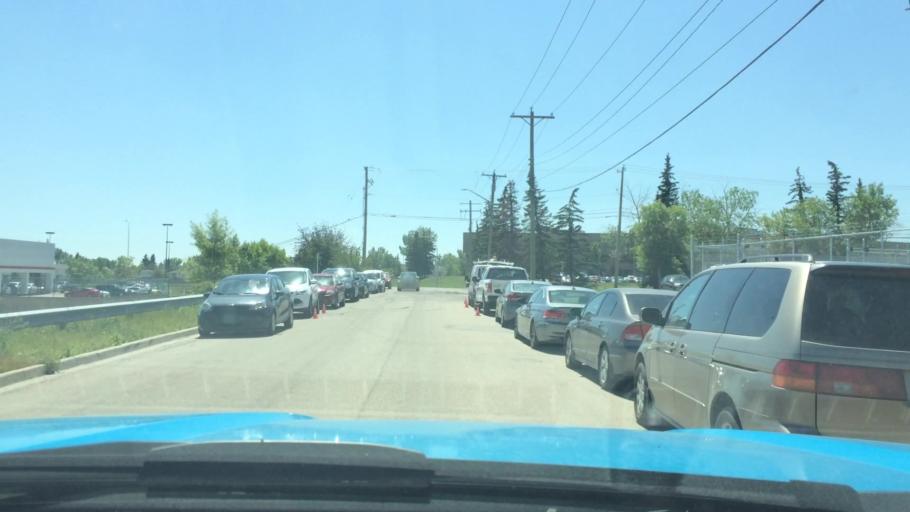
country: CA
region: Alberta
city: Calgary
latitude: 51.0532
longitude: -113.9895
